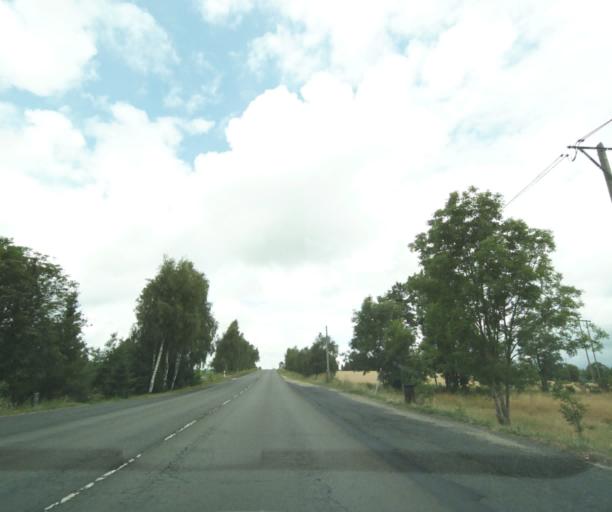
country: FR
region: Languedoc-Roussillon
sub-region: Departement de la Lozere
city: Aumont-Aubrac
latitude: 44.7833
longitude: 3.2874
